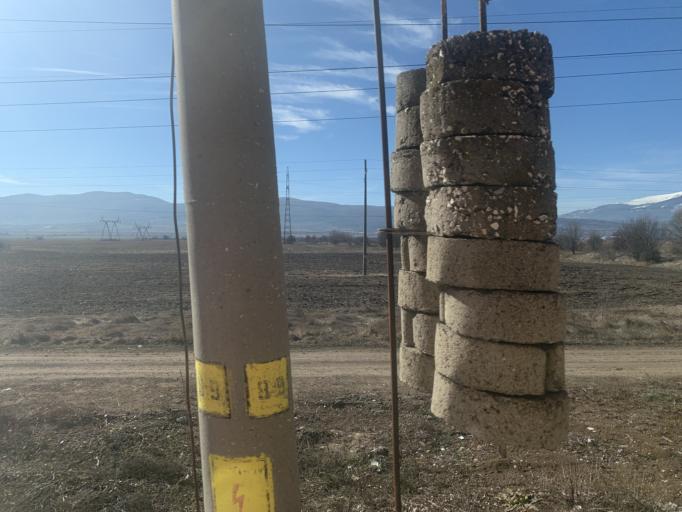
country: BG
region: Sofiya
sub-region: Obshtina Elin Pelin
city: Elin Pelin
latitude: 42.6499
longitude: 23.4806
